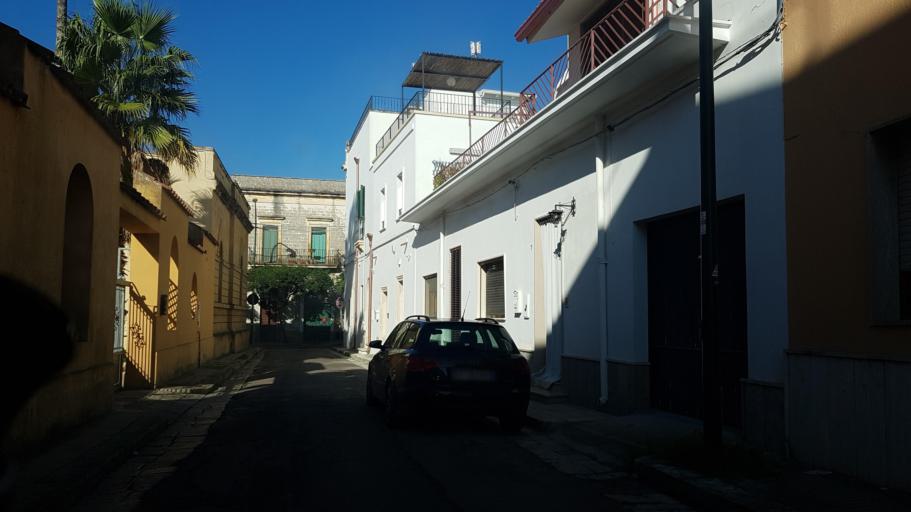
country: IT
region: Apulia
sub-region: Provincia di Lecce
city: Campi Salentina
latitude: 40.3977
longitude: 18.0188
